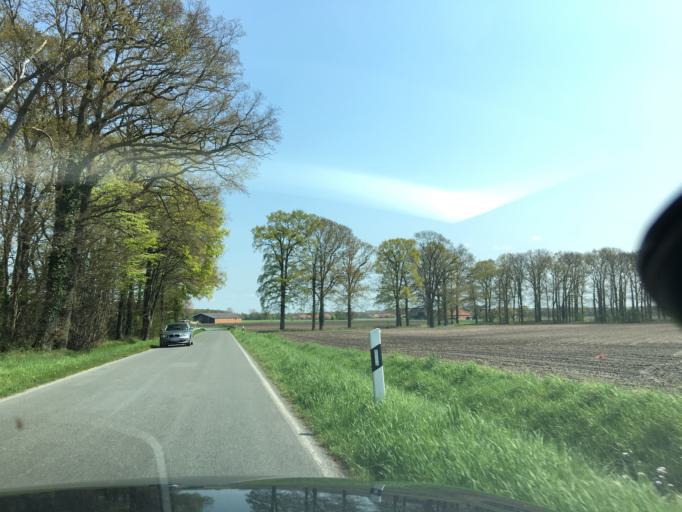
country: DE
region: North Rhine-Westphalia
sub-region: Regierungsbezirk Munster
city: Senden
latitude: 51.8516
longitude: 7.5148
